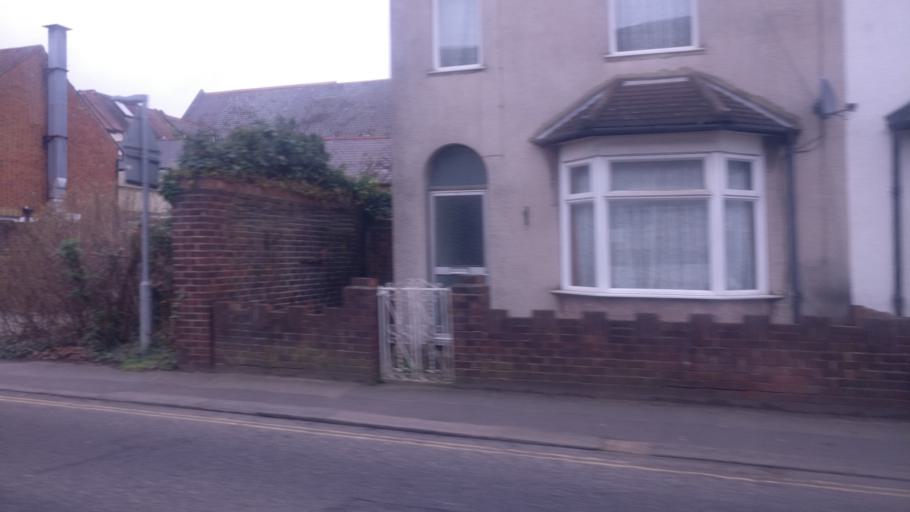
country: GB
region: England
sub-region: Surrey
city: Chertsey
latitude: 51.3880
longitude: -0.5073
